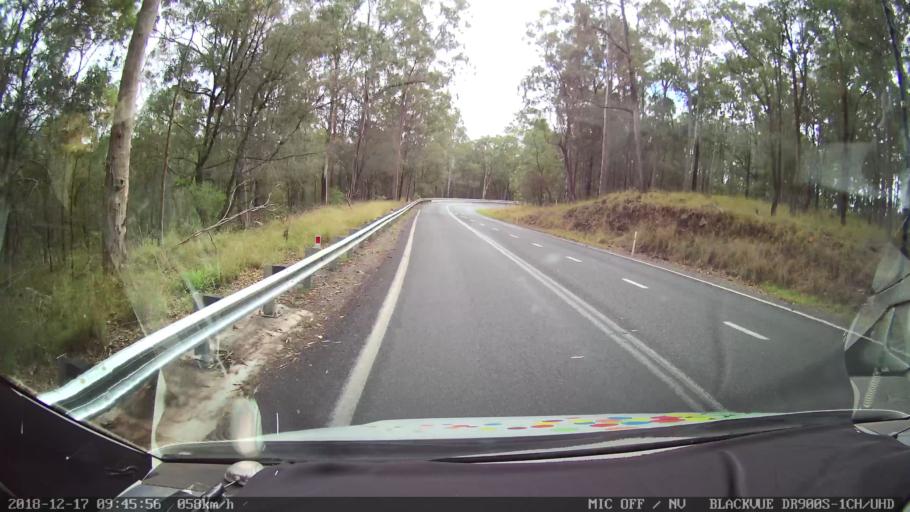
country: AU
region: New South Wales
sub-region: Tenterfield Municipality
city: Carrolls Creek
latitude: -28.9250
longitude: 152.3338
